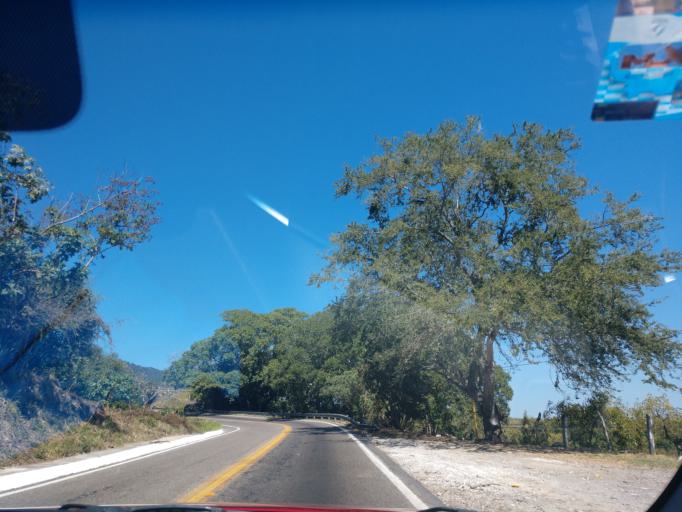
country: MX
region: Nayarit
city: Xalisco
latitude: 21.3710
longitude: -104.9033
